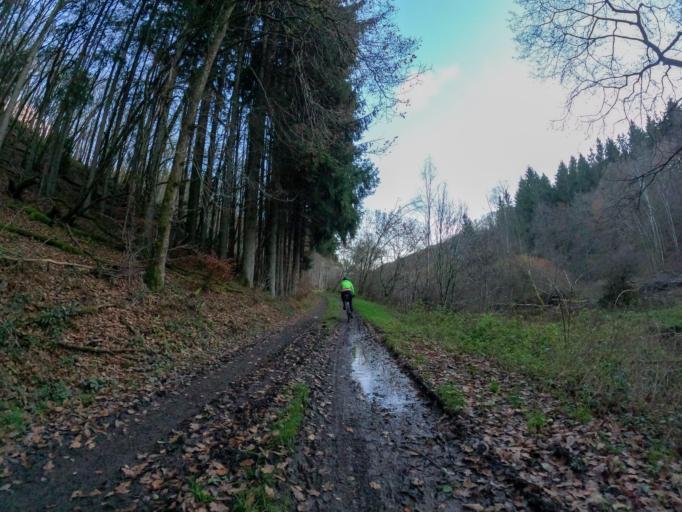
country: LU
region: Diekirch
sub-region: Canton de Wiltz
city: Bavigne
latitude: 49.9411
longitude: 5.8343
